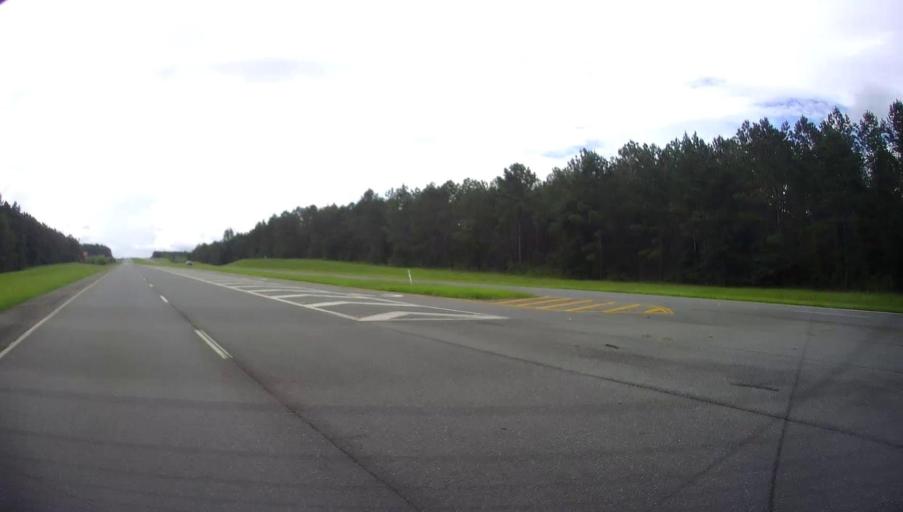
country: US
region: Georgia
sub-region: Schley County
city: Ellaville
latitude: 32.2754
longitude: -84.2980
